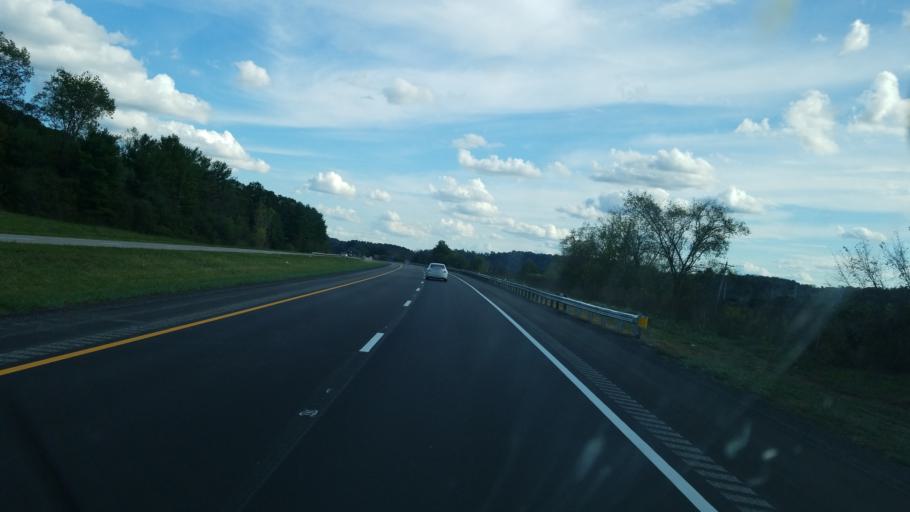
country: US
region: Ohio
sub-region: Noble County
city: Caldwell
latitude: 39.6825
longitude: -81.4930
